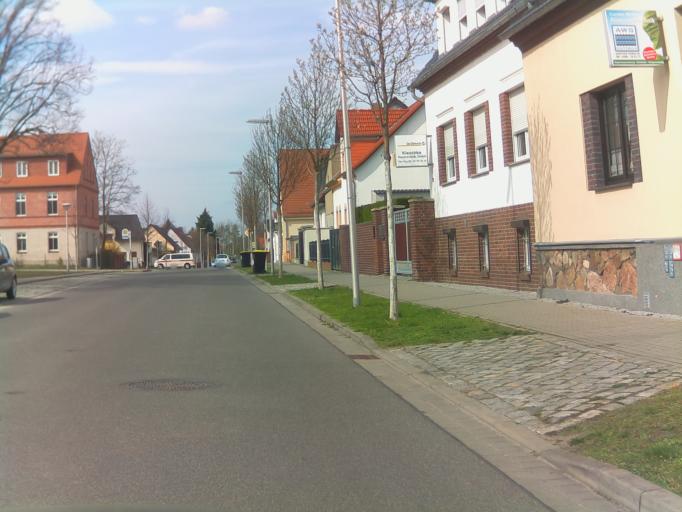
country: DE
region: Brandenburg
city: Cottbus
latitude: 51.7577
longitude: 14.3008
